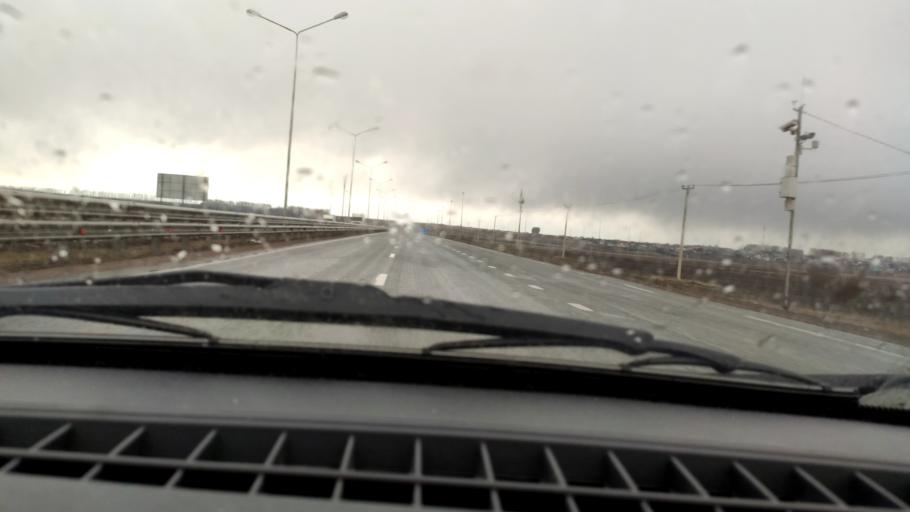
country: RU
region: Bashkortostan
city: Kushnarenkovo
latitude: 55.0736
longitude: 55.2861
